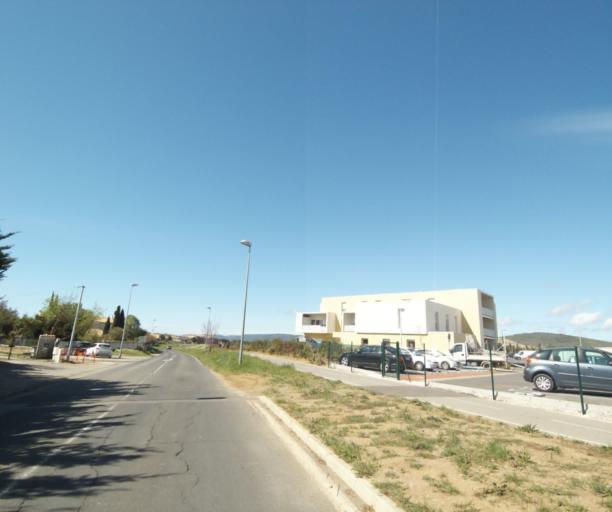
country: FR
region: Languedoc-Roussillon
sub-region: Departement de l'Herault
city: Villeneuve-les-Maguelone
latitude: 43.5324
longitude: 3.8521
